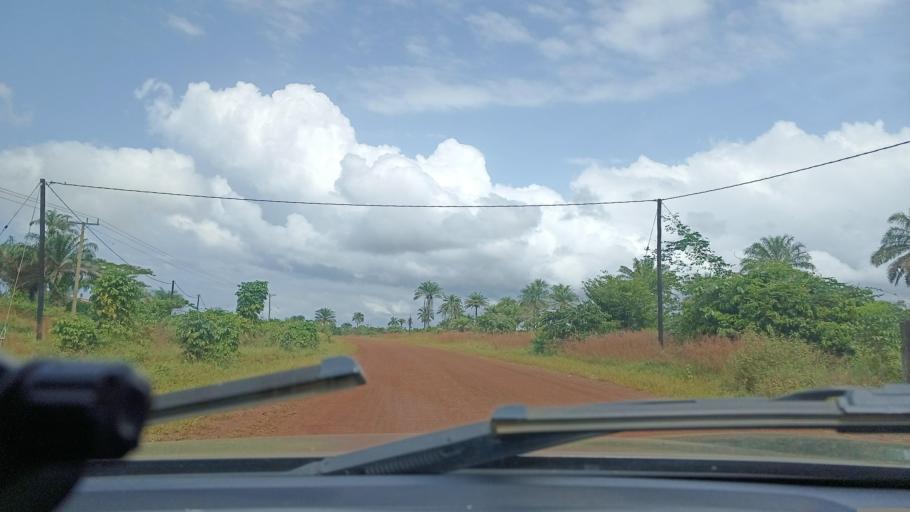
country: LR
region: Grand Cape Mount
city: Robertsport
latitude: 6.7456
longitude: -11.3390
